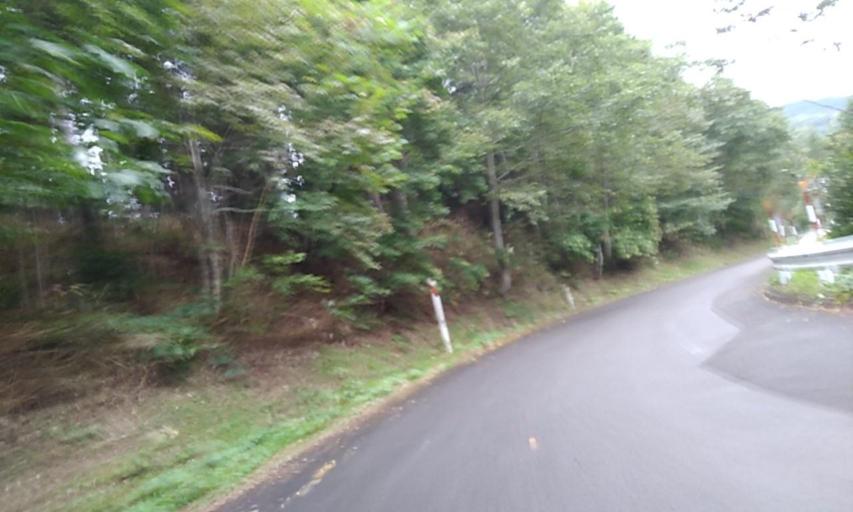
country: JP
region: Hokkaido
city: Bihoro
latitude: 43.5657
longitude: 144.1866
